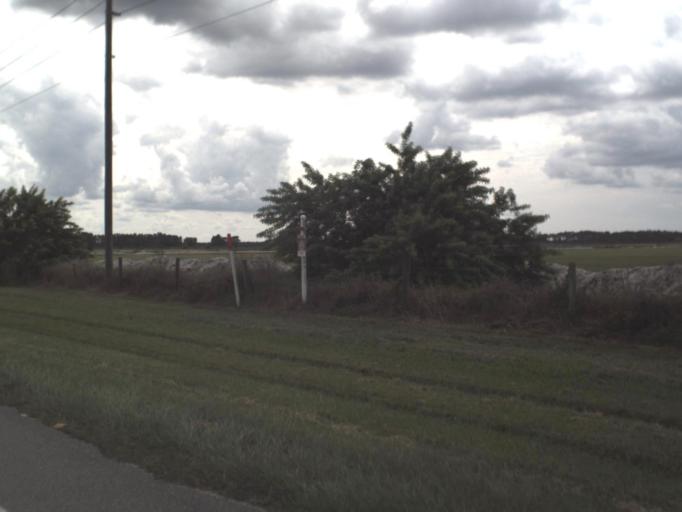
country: US
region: Florida
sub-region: DeSoto County
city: Nocatee
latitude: 26.9965
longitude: -81.7605
